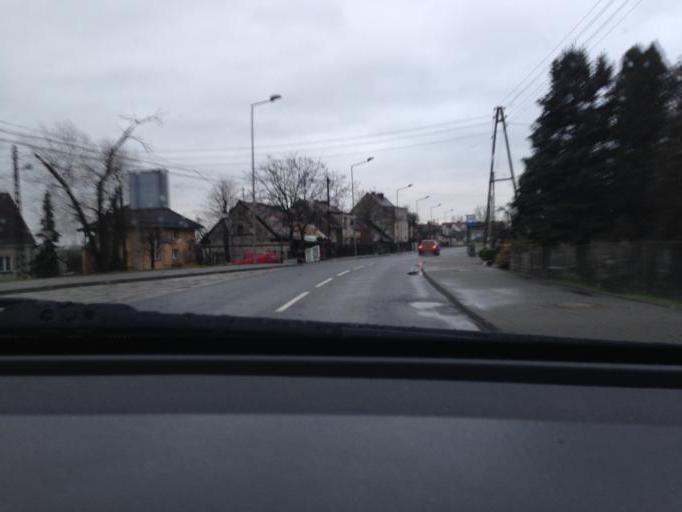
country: PL
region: Opole Voivodeship
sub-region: Powiat opolski
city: Opole
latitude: 50.6901
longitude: 17.9502
